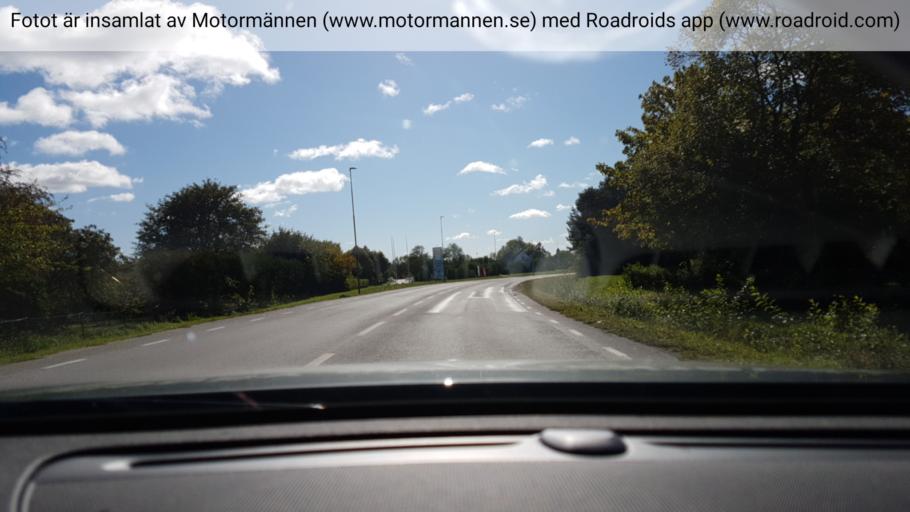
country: SE
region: Gotland
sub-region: Gotland
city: Slite
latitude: 57.7046
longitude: 18.7957
